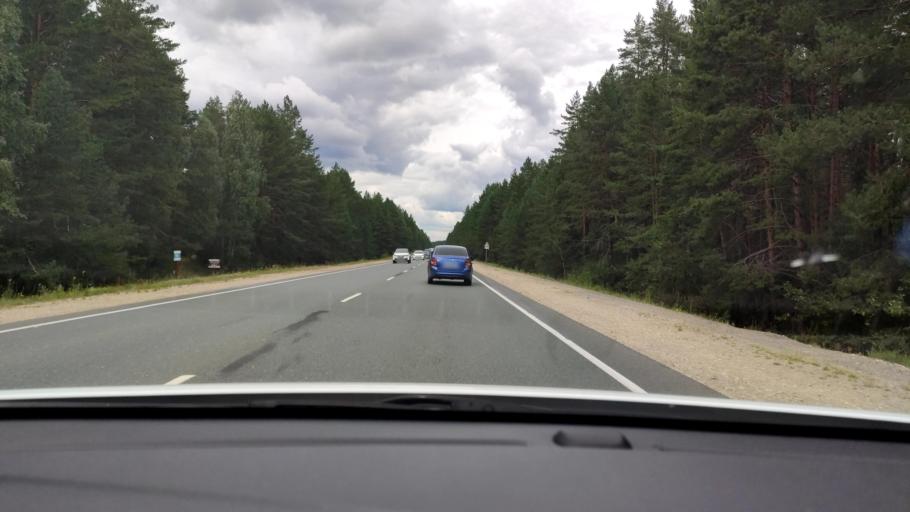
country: RU
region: Mariy-El
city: Pomary
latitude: 56.0441
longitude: 48.3771
